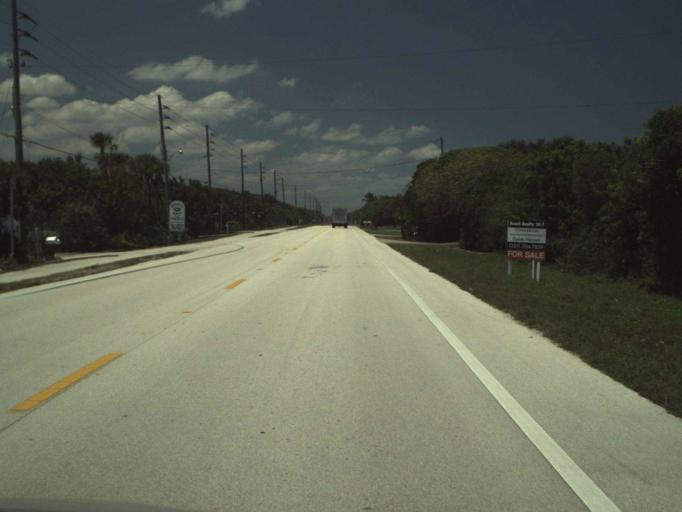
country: US
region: Florida
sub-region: Brevard County
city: Micco
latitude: 27.8868
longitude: -80.4625
